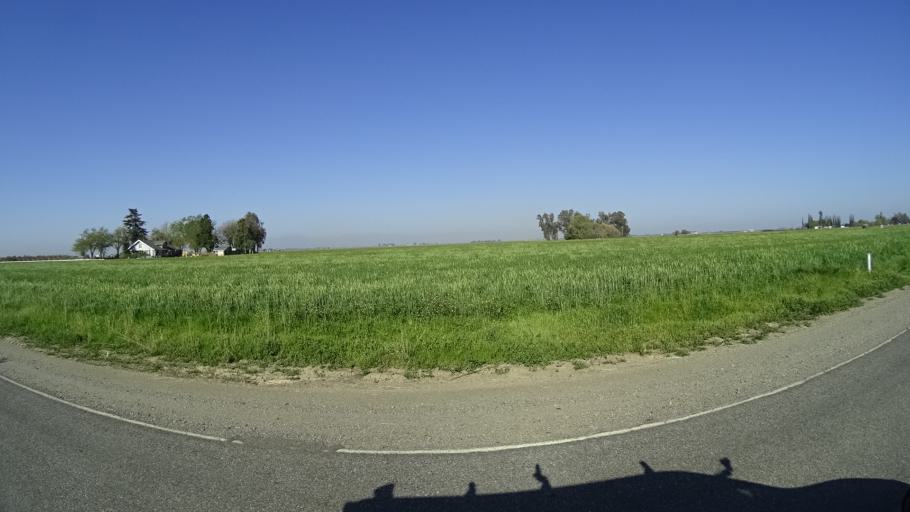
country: US
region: California
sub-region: Glenn County
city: Willows
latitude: 39.5551
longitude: -122.1020
